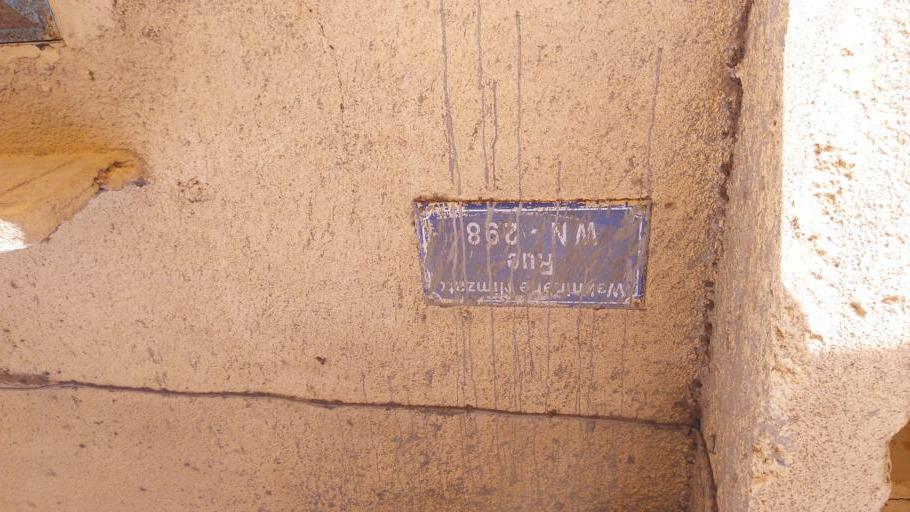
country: SN
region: Dakar
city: Pikine
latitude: 14.7777
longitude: -17.3766
